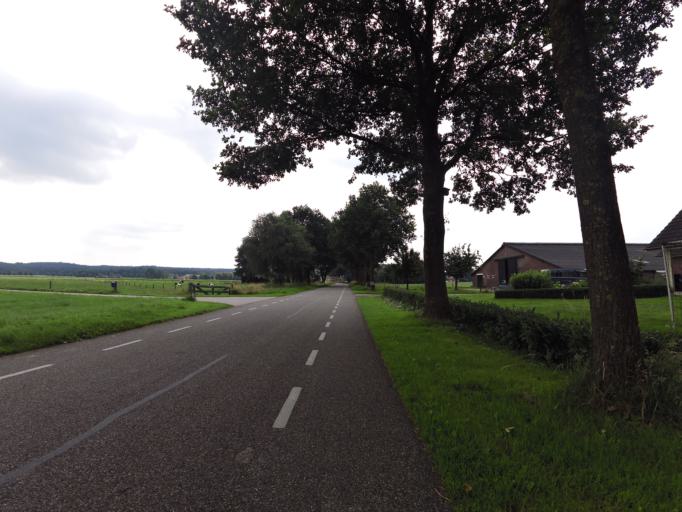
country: NL
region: Gelderland
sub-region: Gemeente Montferland
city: s-Heerenberg
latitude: 51.9342
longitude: 6.2039
